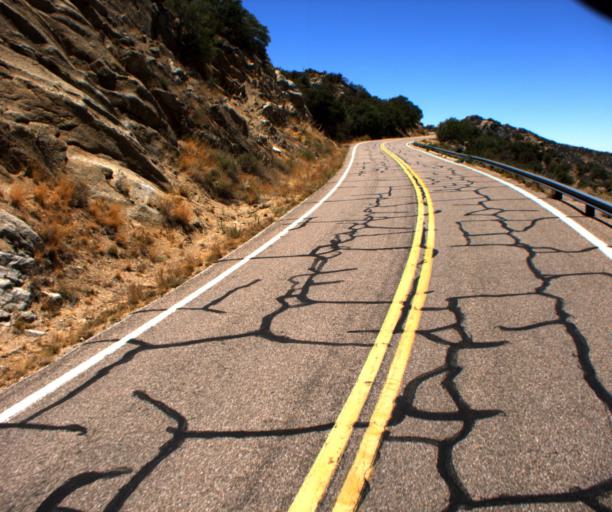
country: US
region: Arizona
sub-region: Pima County
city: Sells
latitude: 31.9729
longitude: -111.6180
